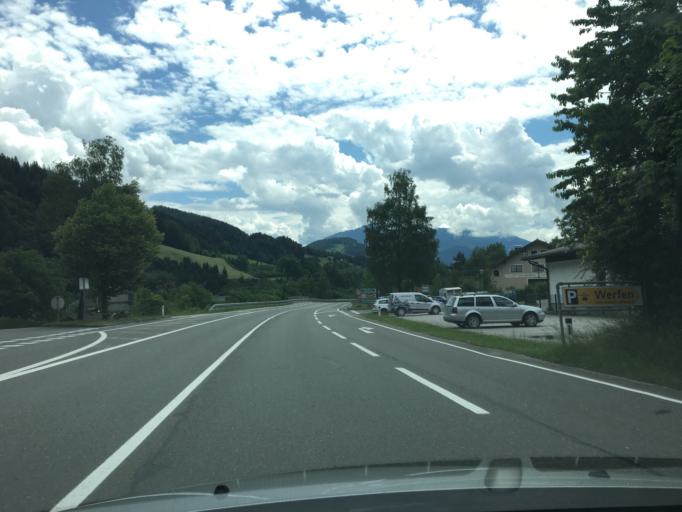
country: AT
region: Salzburg
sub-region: Politischer Bezirk Sankt Johann im Pongau
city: Werfen
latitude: 47.4767
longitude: 13.1904
